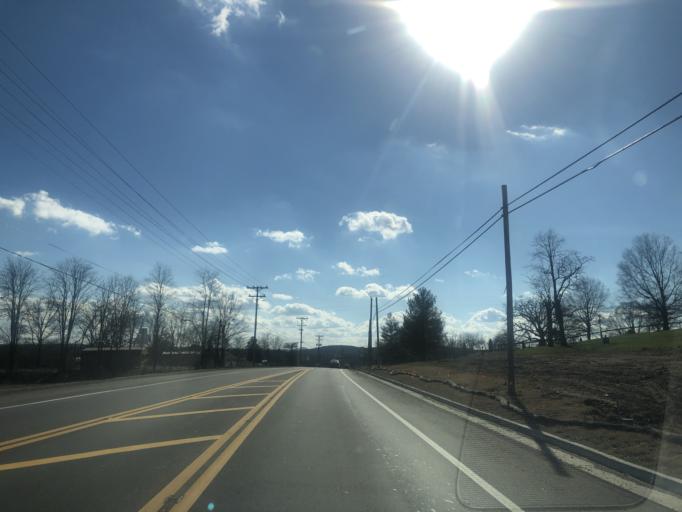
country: US
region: Tennessee
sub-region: Williamson County
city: Nolensville
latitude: 35.8532
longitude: -86.6591
